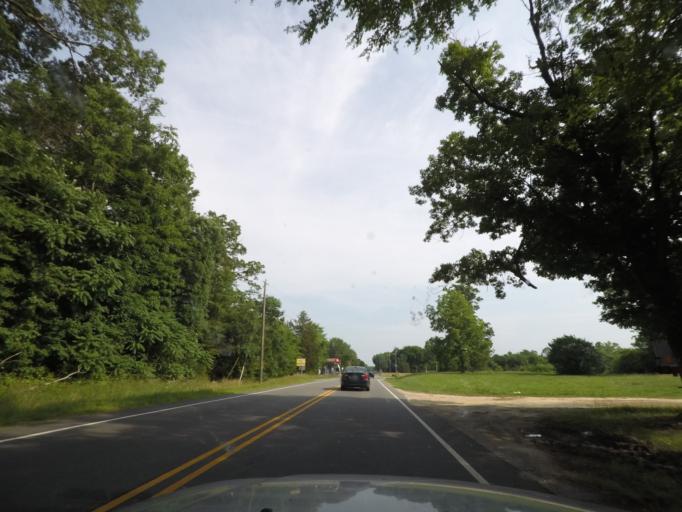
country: US
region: Virginia
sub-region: Prince Edward County
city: Hampden Sydney
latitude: 37.2310
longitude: -78.4430
